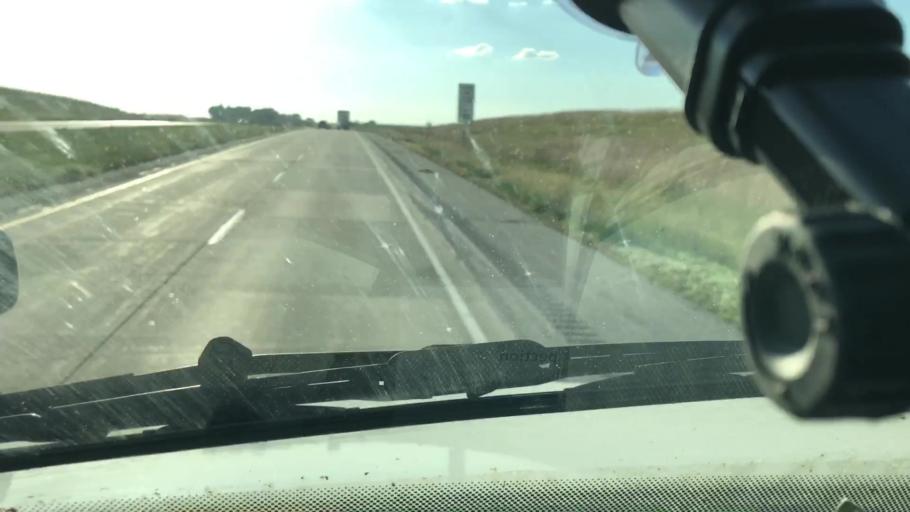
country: US
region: Iowa
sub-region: Pottawattamie County
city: Avoca
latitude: 41.4990
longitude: -95.4632
